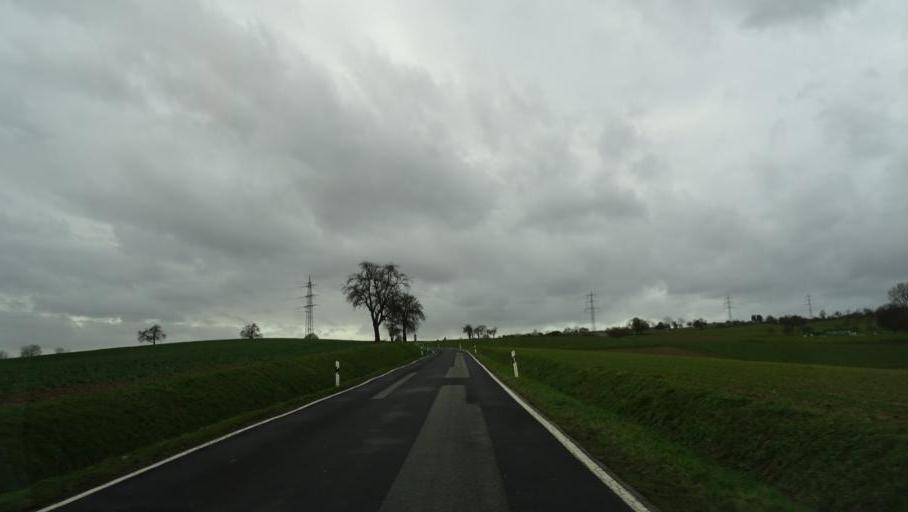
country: DE
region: Baden-Wuerttemberg
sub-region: Karlsruhe Region
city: Neunkirchen
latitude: 49.3838
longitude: 9.0264
